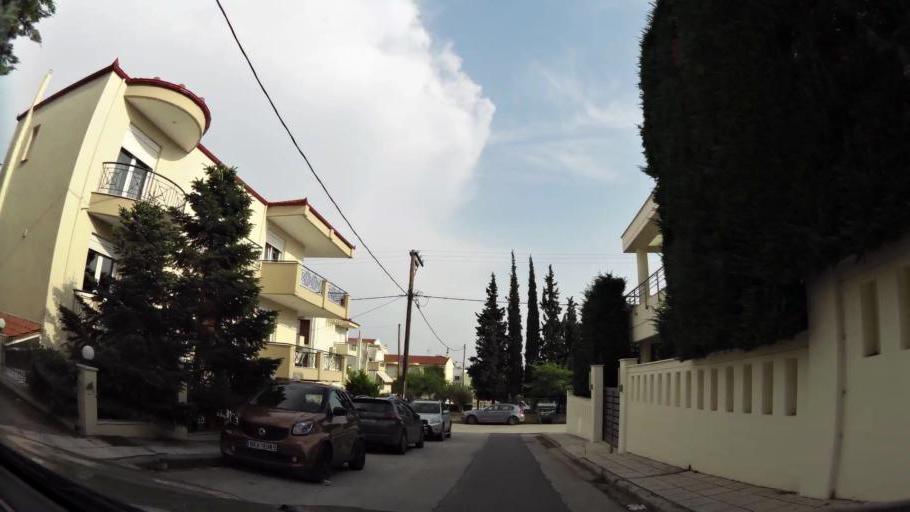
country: GR
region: Central Macedonia
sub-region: Nomos Thessalonikis
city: Oraiokastro
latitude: 40.7235
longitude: 22.9237
